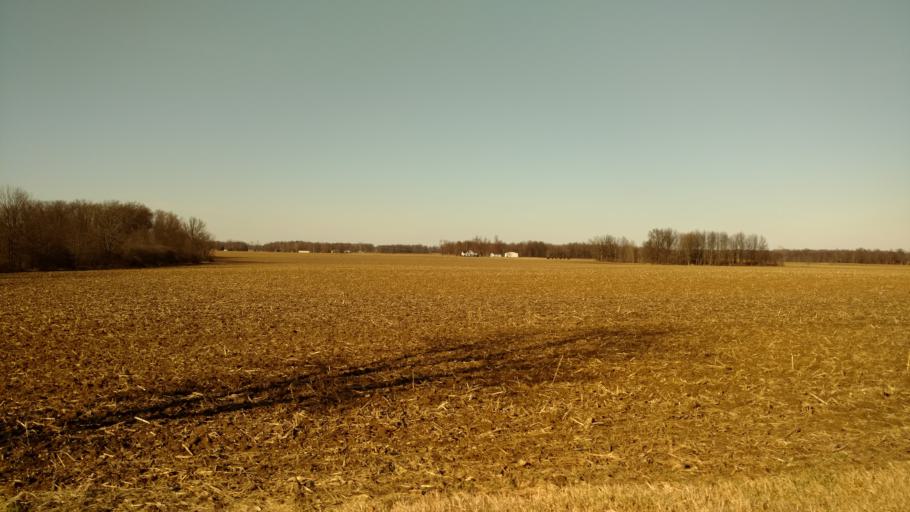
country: US
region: Ohio
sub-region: Crawford County
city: Galion
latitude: 40.6976
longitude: -82.8729
